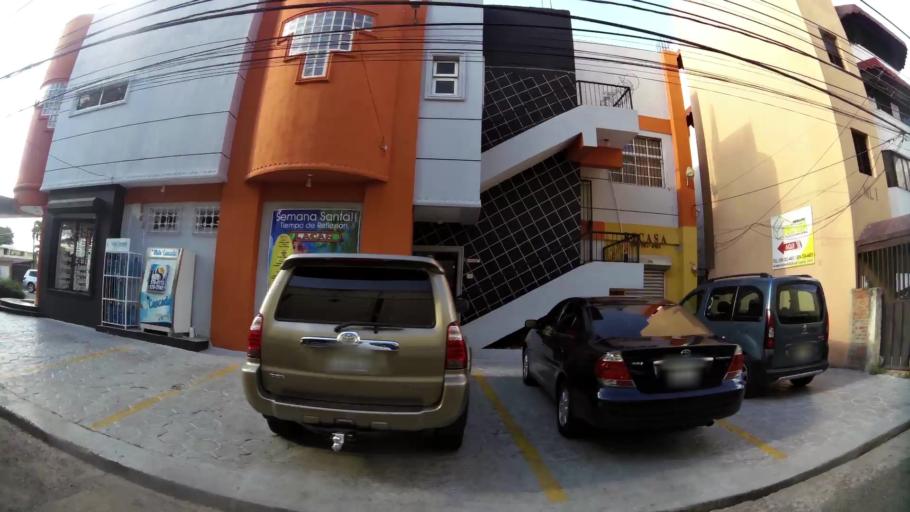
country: DO
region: Santiago
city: Santiago de los Caballeros
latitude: 19.4598
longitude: -70.6943
